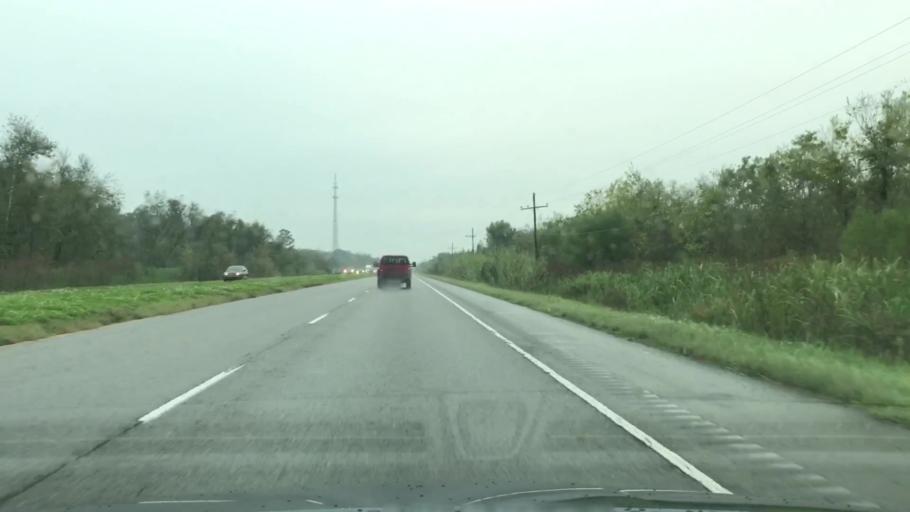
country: US
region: Louisiana
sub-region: Saint Charles Parish
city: Des Allemands
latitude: 29.7877
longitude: -90.5166
